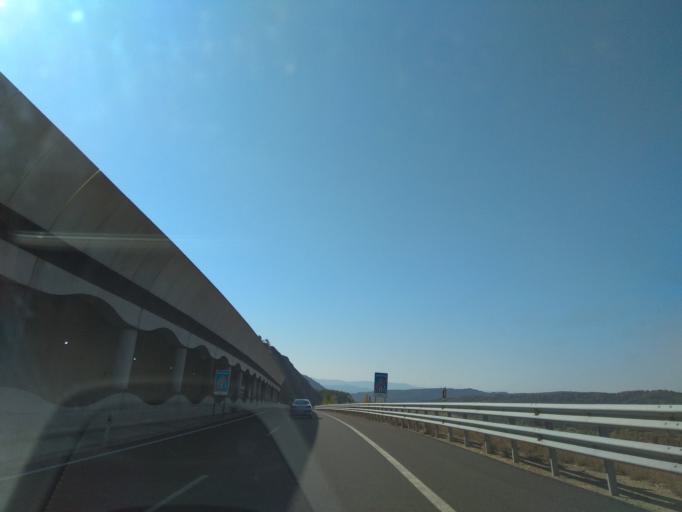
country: ES
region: Aragon
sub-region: Provincia de Huesca
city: Sabinanigo
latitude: 42.4946
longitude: -0.3646
